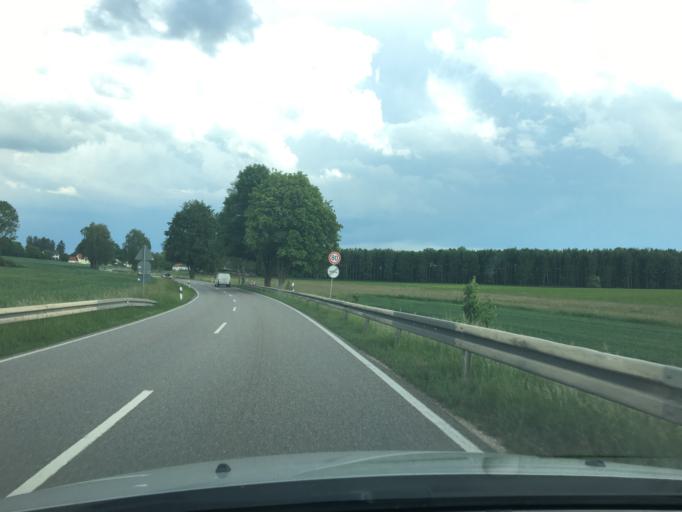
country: DE
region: Bavaria
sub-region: Upper Bavaria
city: Hebertshausen
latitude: 48.3184
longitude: 11.4852
